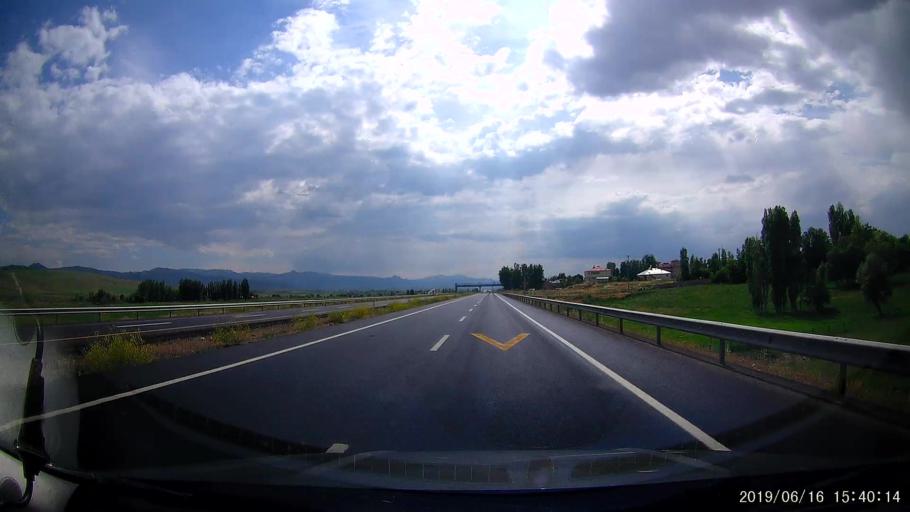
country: TR
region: Erzurum
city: Koprukoy
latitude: 39.9683
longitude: 41.8772
